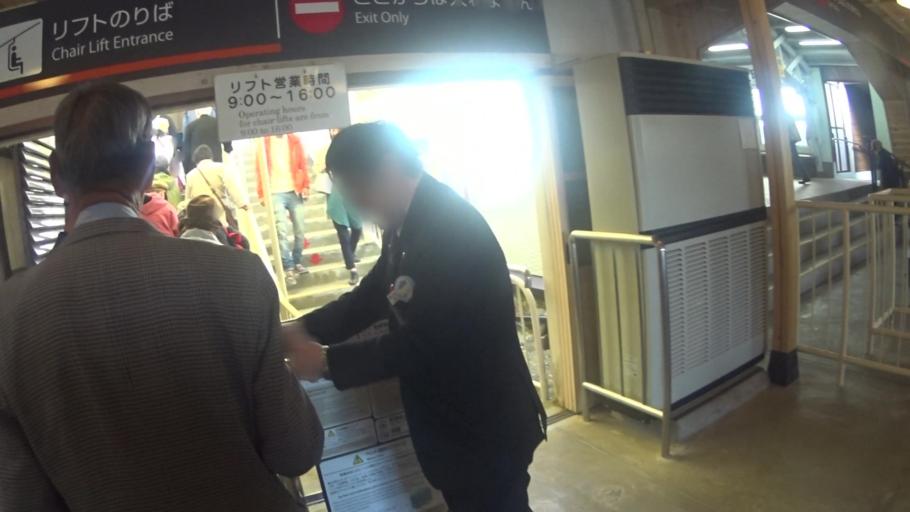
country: JP
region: Kyoto
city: Miyazu
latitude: 35.5833
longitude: 135.1950
